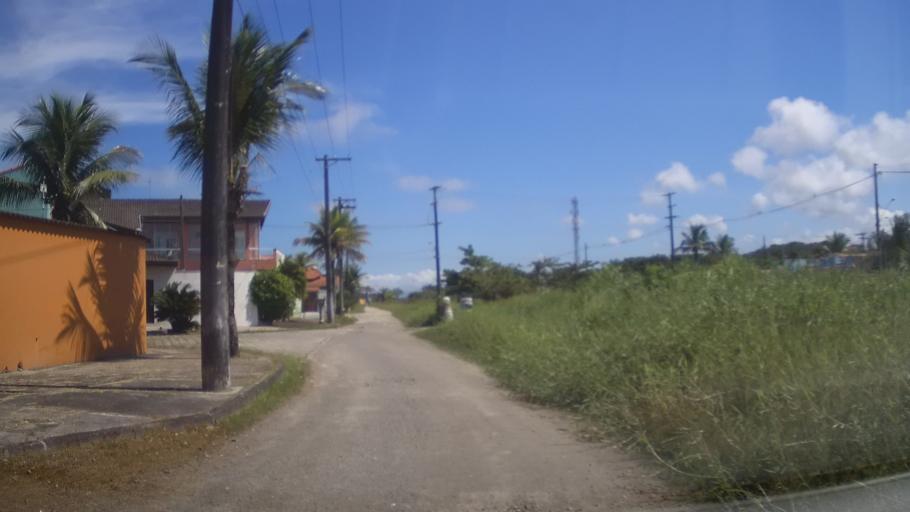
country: BR
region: Sao Paulo
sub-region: Itanhaem
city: Itanhaem
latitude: -24.1416
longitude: -46.7117
